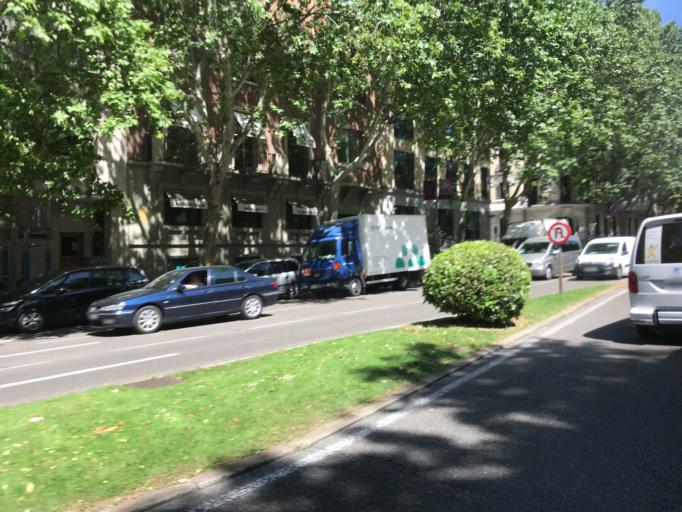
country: ES
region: Madrid
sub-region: Provincia de Madrid
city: Retiro
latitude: 40.4128
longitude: -3.6888
